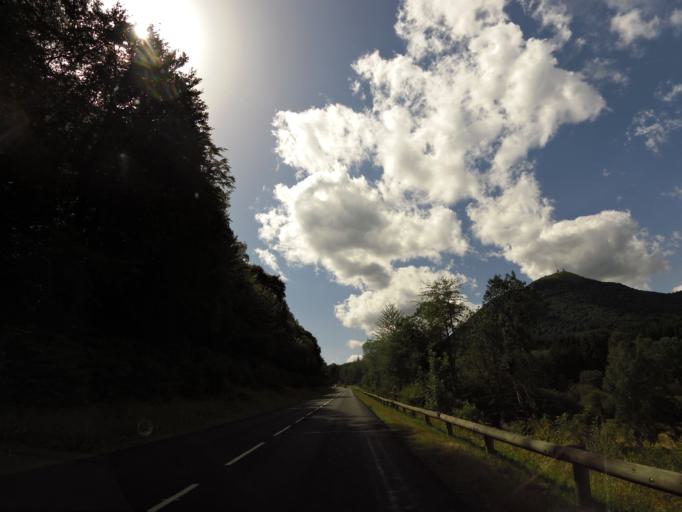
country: FR
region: Auvergne
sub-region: Departement du Puy-de-Dome
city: Orcines
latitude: 45.7610
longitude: 2.9871
